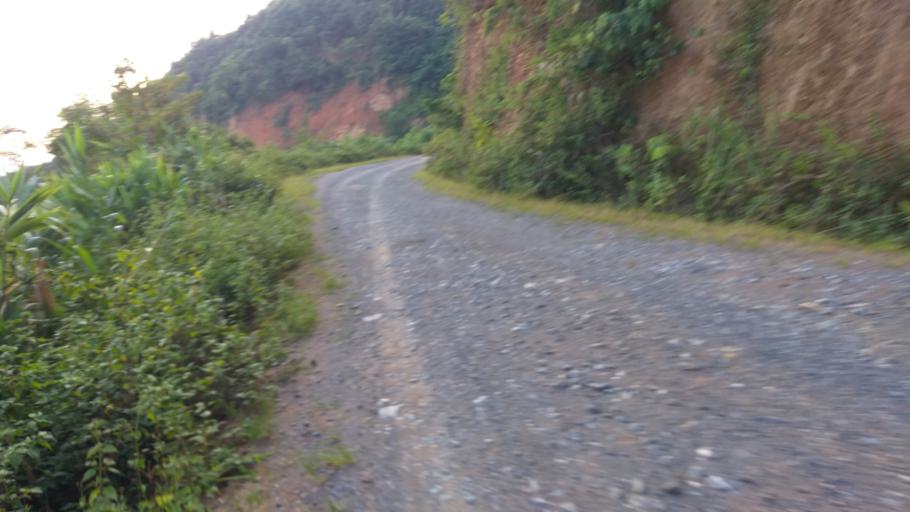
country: LA
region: Phongsali
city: Khoa
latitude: 21.1979
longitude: 102.5699
